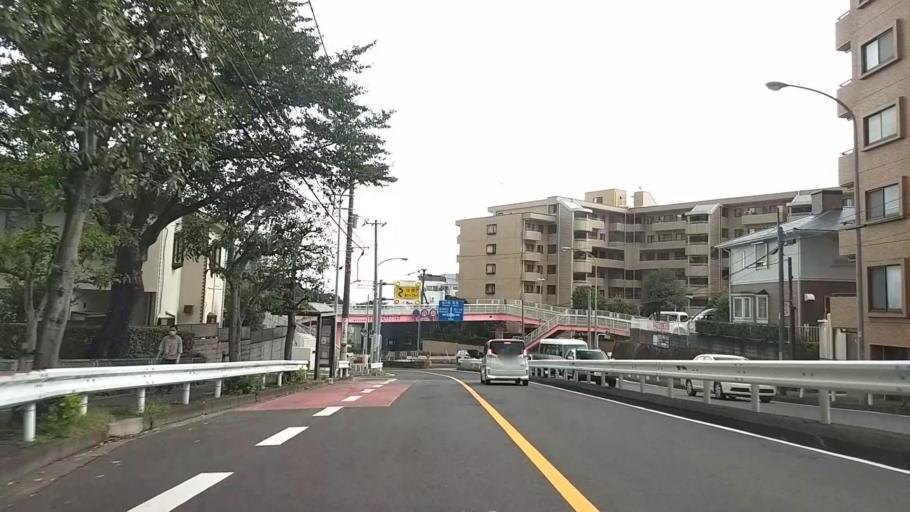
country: JP
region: Kanagawa
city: Yokohama
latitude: 35.4691
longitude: 139.6082
